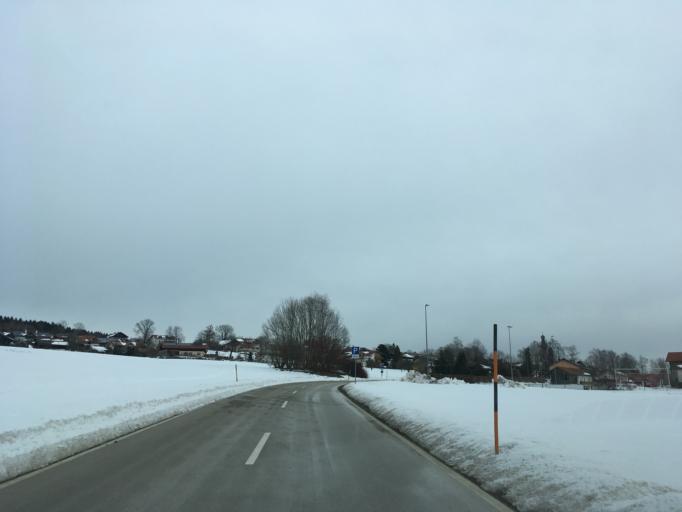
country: DE
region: Bavaria
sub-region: Upper Bavaria
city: Schnaitsee
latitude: 48.0664
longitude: 12.3615
